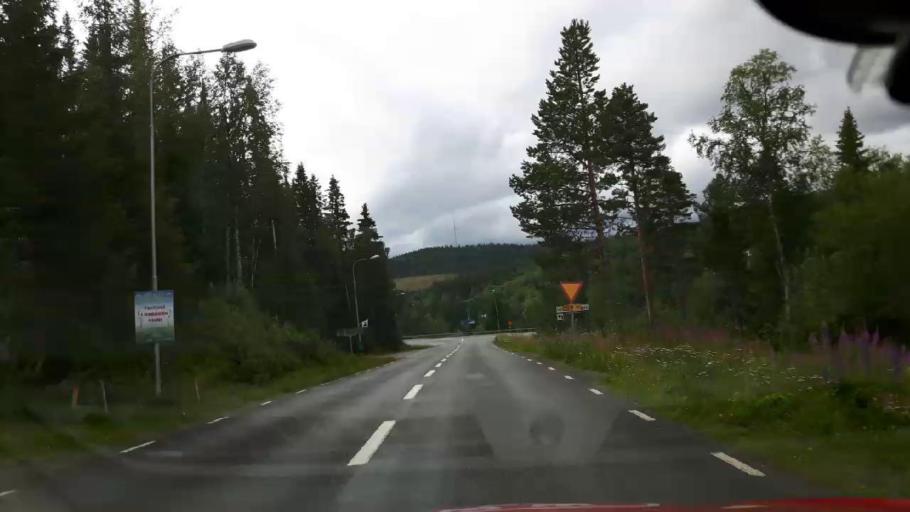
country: NO
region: Nord-Trondelag
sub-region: Lierne
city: Sandvika
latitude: 64.4980
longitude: 14.1494
